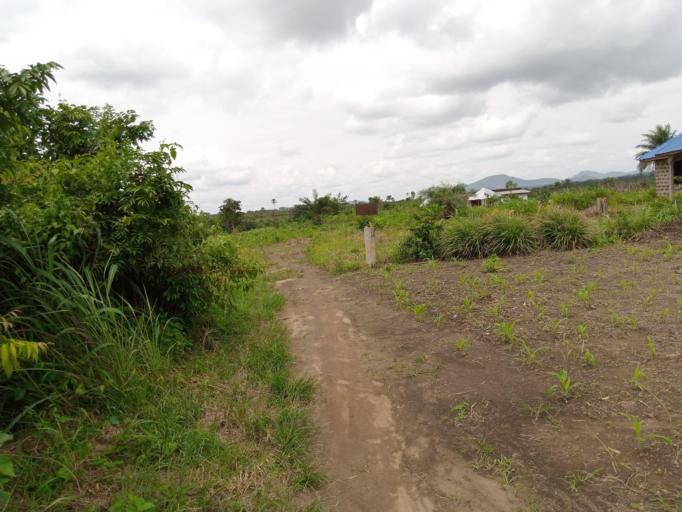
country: SL
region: Southern Province
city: Moyamba
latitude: 8.1692
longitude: -12.4143
